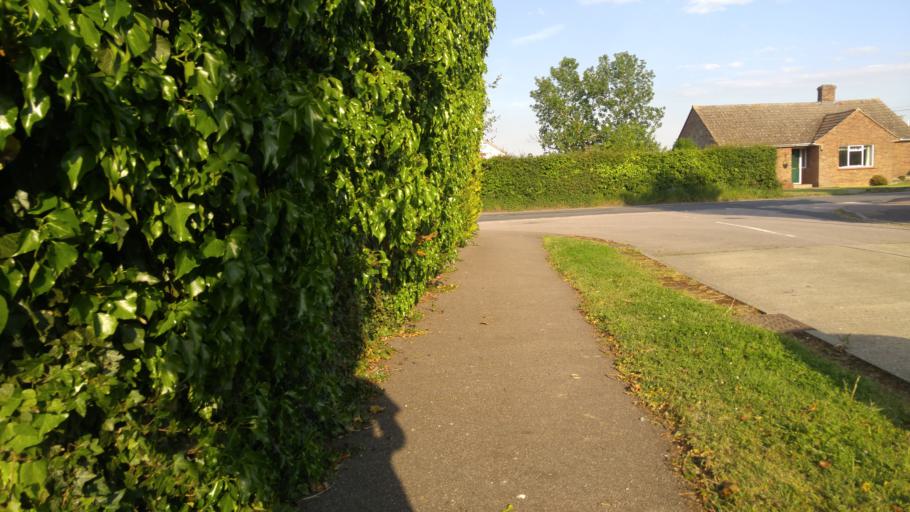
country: GB
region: England
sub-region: Essex
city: Eight Ash Green
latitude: 51.9219
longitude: 0.8031
